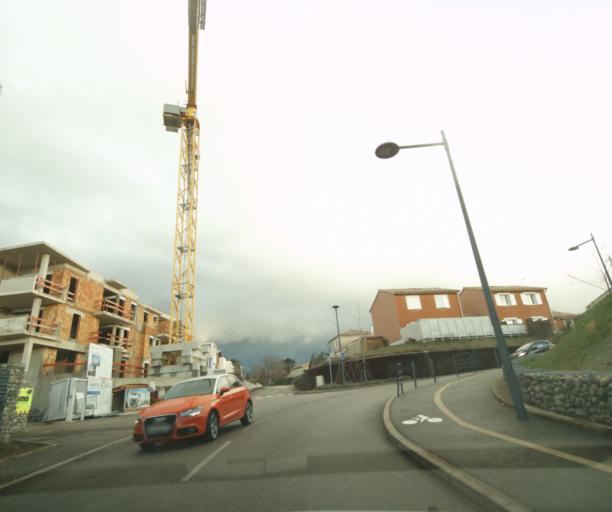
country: FR
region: Rhone-Alpes
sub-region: Departement de la Drome
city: Bourg-les-Valence
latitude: 44.9480
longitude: 4.9046
